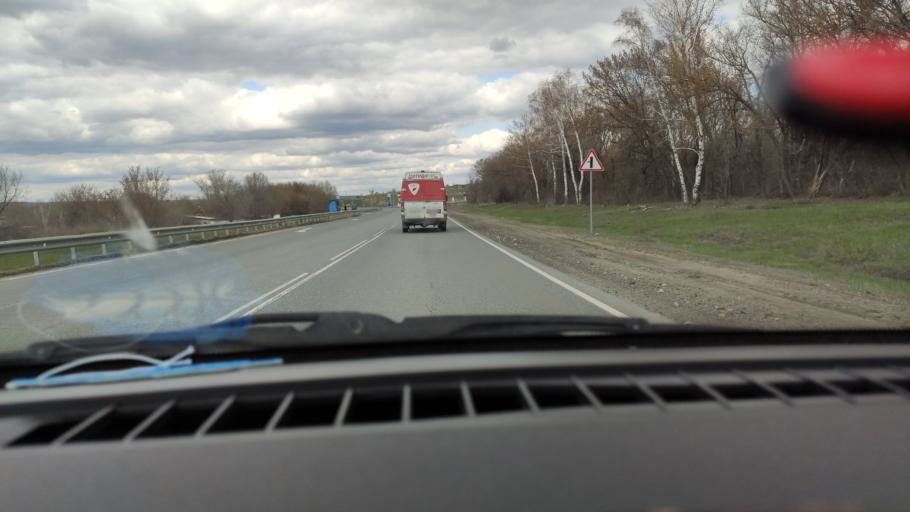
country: RU
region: Saratov
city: Tersa
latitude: 52.0940
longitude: 47.5413
